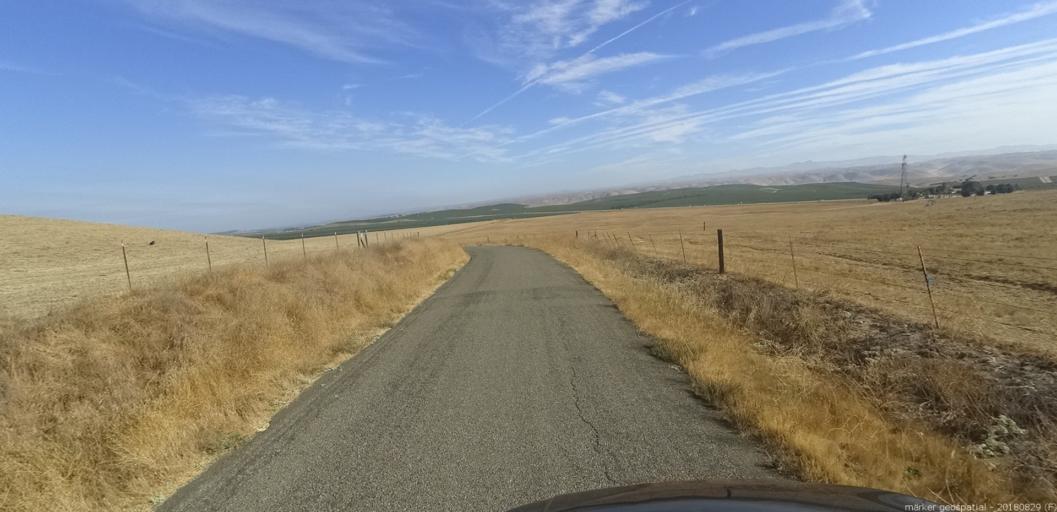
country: US
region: California
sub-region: Monterey County
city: King City
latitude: 36.0490
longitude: -120.9779
